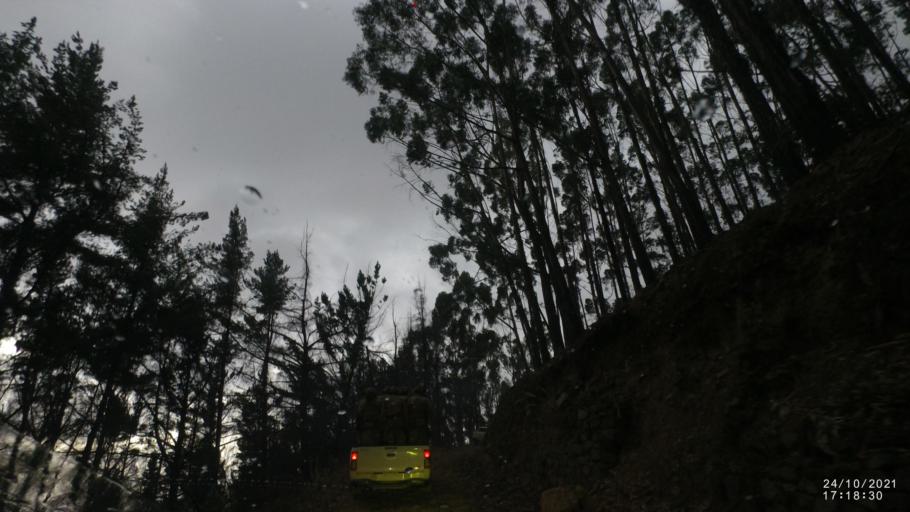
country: BO
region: Cochabamba
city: Cochabamba
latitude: -17.3294
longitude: -66.1372
